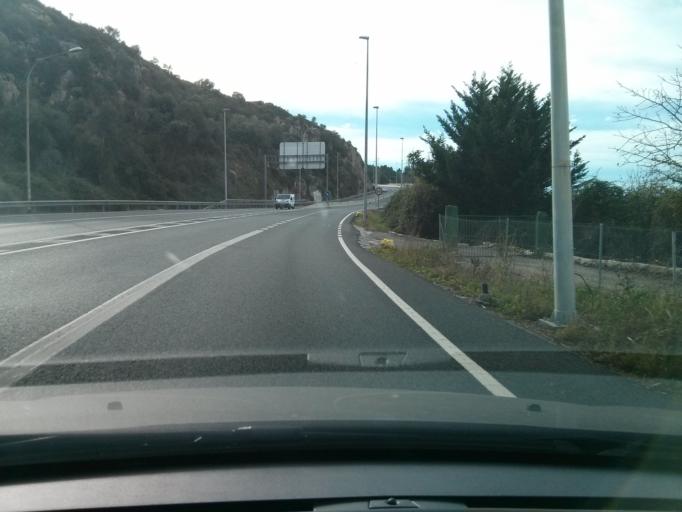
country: ES
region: Catalonia
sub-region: Provincia de Tarragona
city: Tarragona
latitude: 41.1396
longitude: 1.2391
